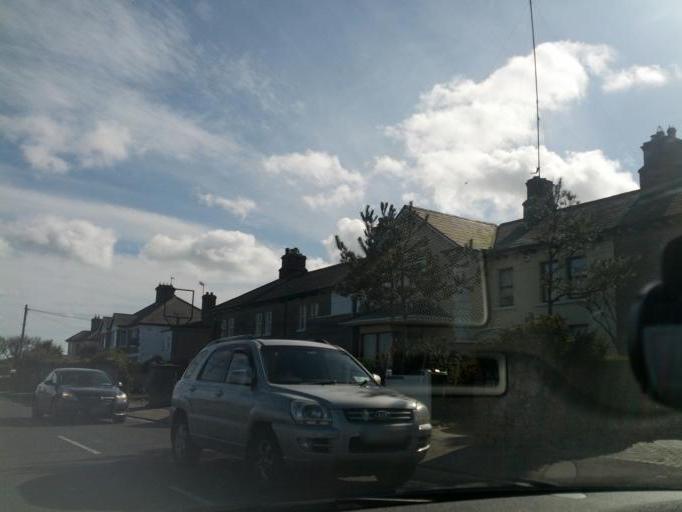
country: IE
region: Leinster
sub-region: Fingal County
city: Baldoyle
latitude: 53.3966
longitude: -6.1253
